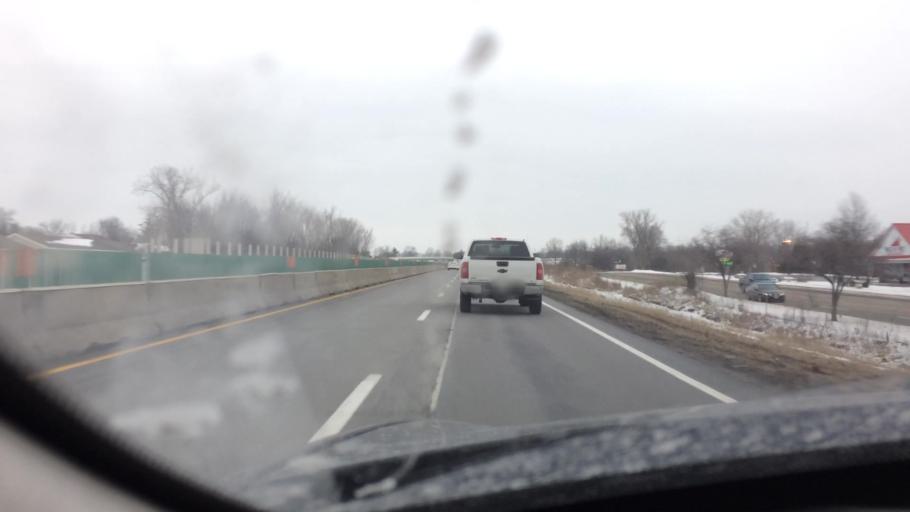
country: US
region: Ohio
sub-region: Hancock County
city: Findlay
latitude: 41.0679
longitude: -83.6638
